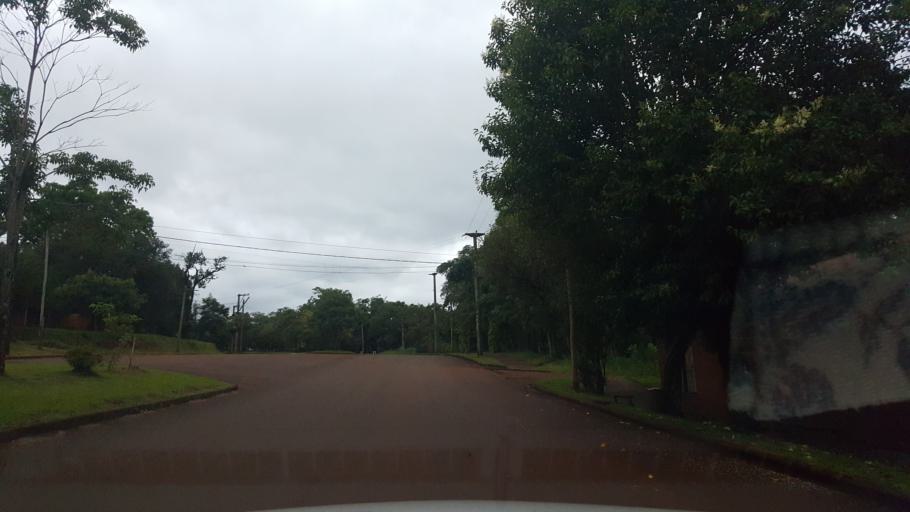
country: AR
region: Misiones
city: Ruiz de Montoya
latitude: -26.9819
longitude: -55.0506
